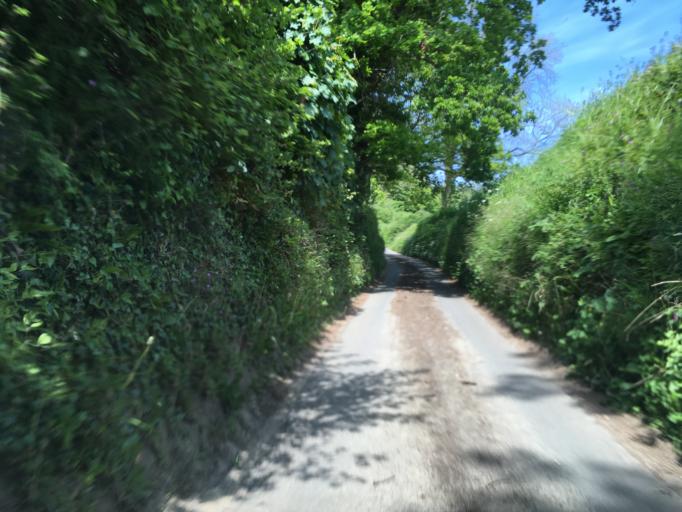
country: GB
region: England
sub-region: Gloucestershire
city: Dursley
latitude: 51.6652
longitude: -2.3379
